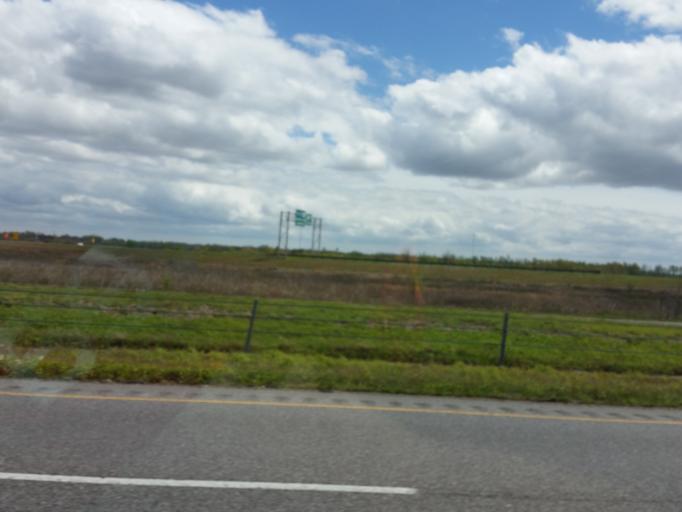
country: US
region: Arkansas
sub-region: Crittenden County
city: Marion
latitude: 35.3892
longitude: -90.2776
